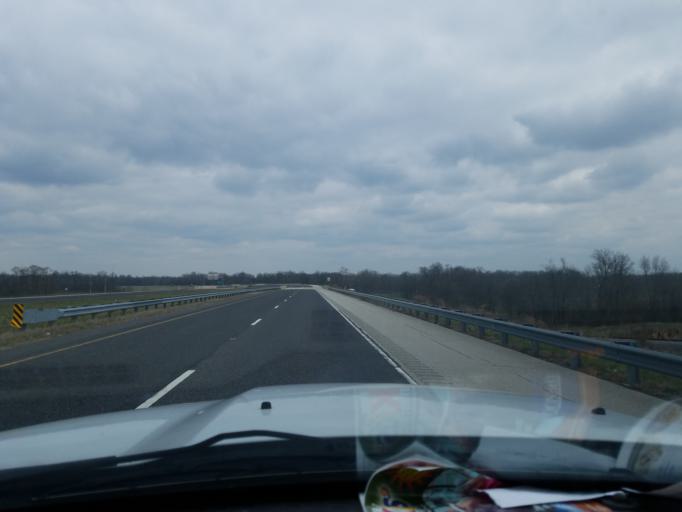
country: US
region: Indiana
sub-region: Vigo County
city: Terre Haute
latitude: 39.3735
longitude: -87.3790
